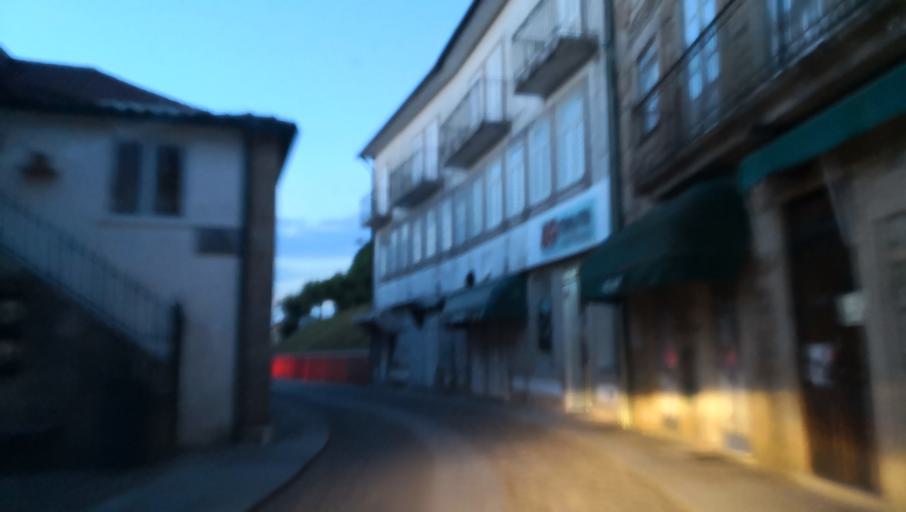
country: PT
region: Viana do Castelo
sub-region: Valenca
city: Valenca
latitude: 42.0278
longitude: -8.6454
